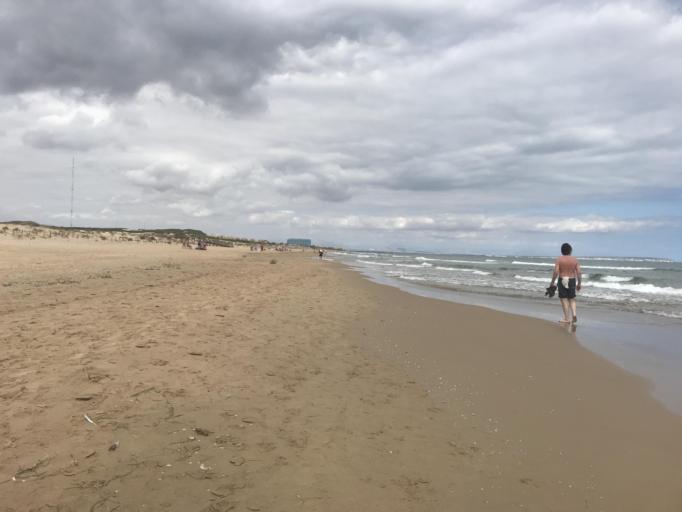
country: ES
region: Valencia
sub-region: Provincia de Alicante
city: Guardamar del Segura
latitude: 38.0451
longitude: -0.6513
